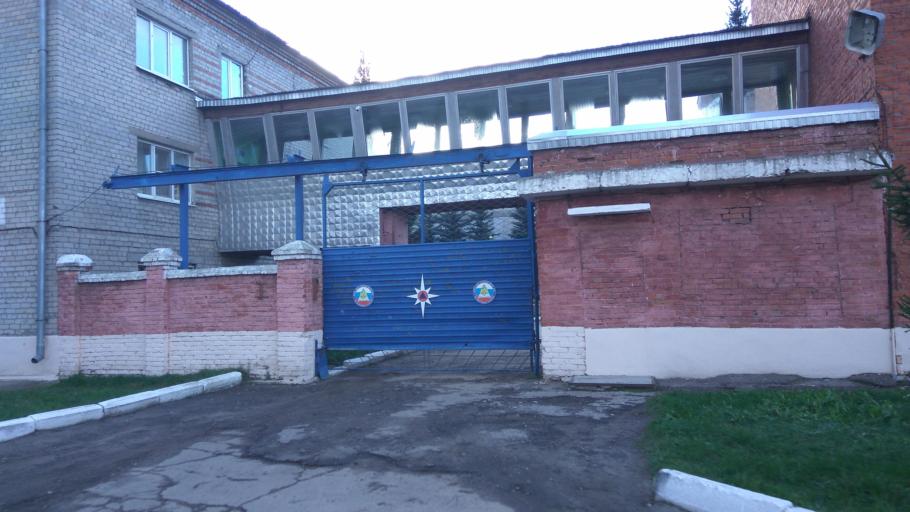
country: RU
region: Tatarstan
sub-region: Gorod Kazan'
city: Kazan
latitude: 55.7329
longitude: 49.1339
